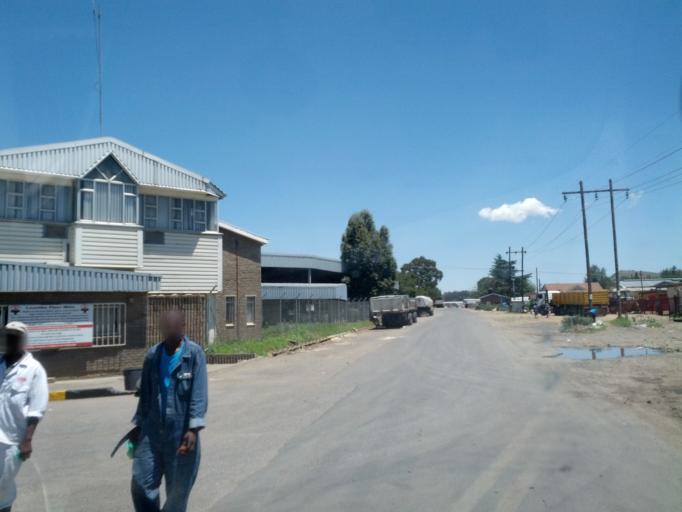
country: LS
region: Maseru
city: Maseru
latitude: -29.2949
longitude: 27.4803
